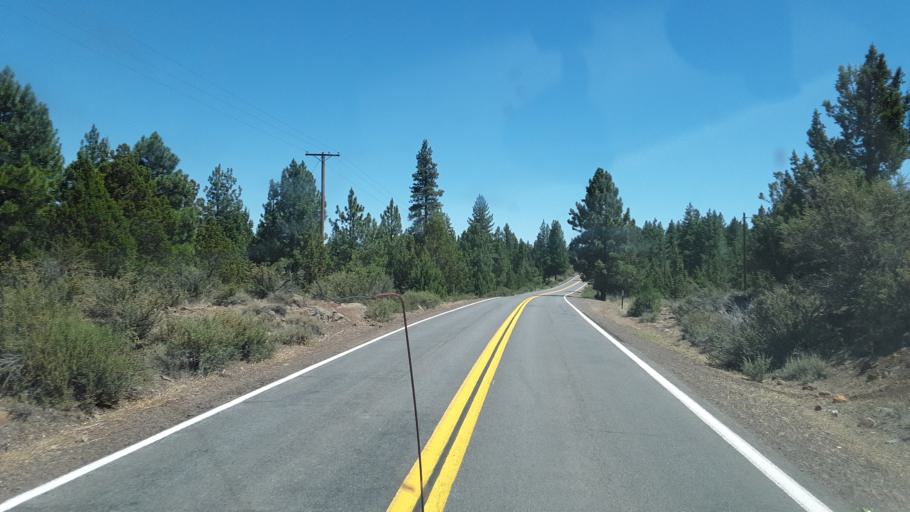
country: US
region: California
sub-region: Lassen County
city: Susanville
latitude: 40.5116
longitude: -120.5745
